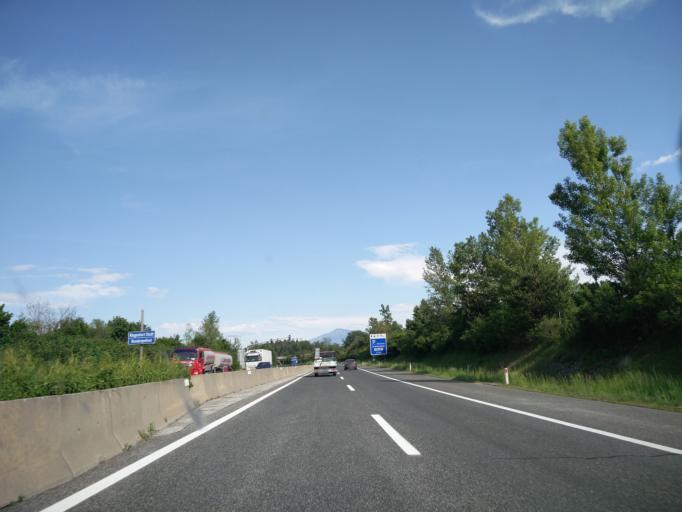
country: AT
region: Carinthia
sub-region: Politischer Bezirk Klagenfurt Land
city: Ebenthal
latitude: 46.6457
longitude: 14.3912
